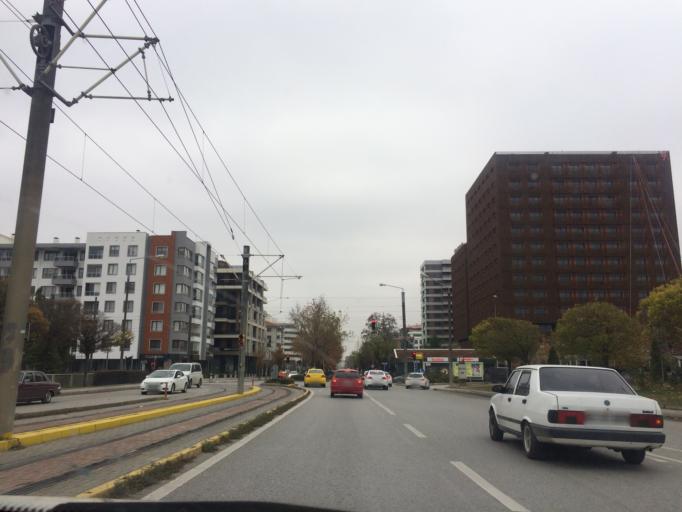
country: TR
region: Eskisehir
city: Eskisehir
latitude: 39.7862
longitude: 30.4986
